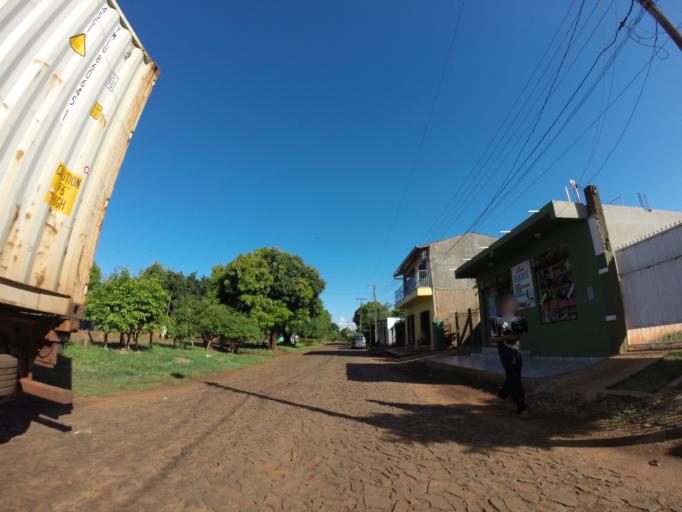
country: PY
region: Alto Parana
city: Ciudad del Este
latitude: -25.3856
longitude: -54.6558
